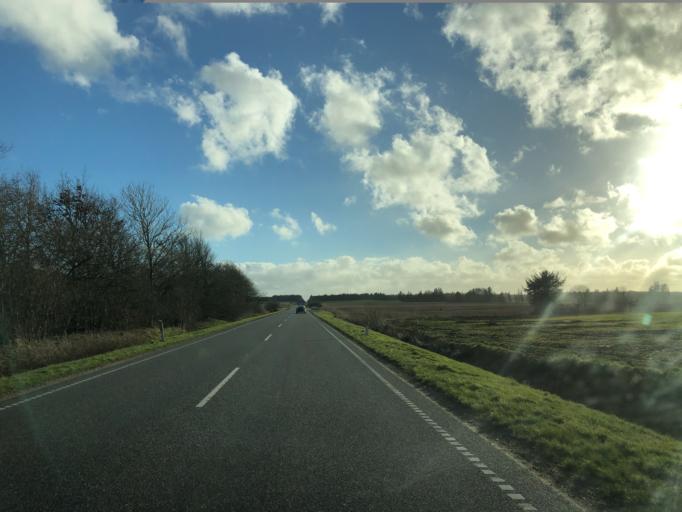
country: DK
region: Central Jutland
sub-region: Herning Kommune
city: Vildbjerg
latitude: 56.1890
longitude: 8.7089
